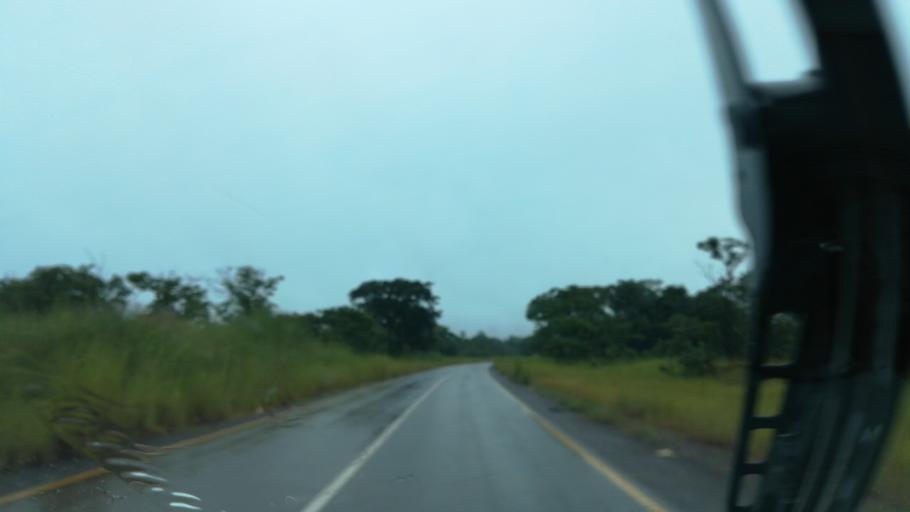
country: ZM
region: Luapula
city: Mwense
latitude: -10.8625
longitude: 28.2236
